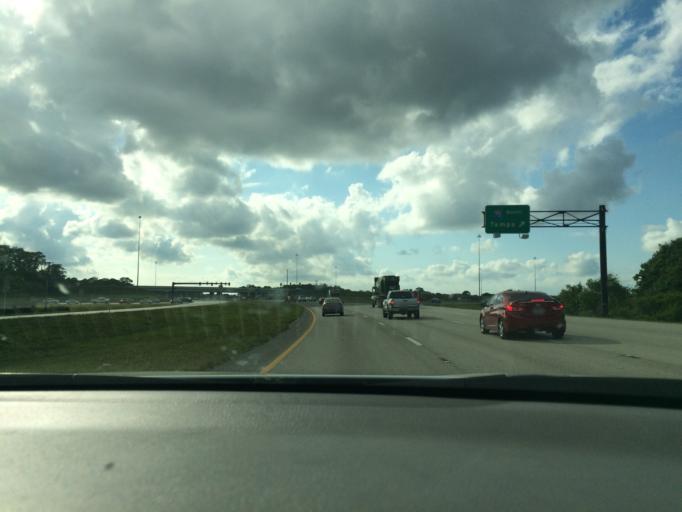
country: US
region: Florida
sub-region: Manatee County
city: Ellenton
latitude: 27.4907
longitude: -82.4681
